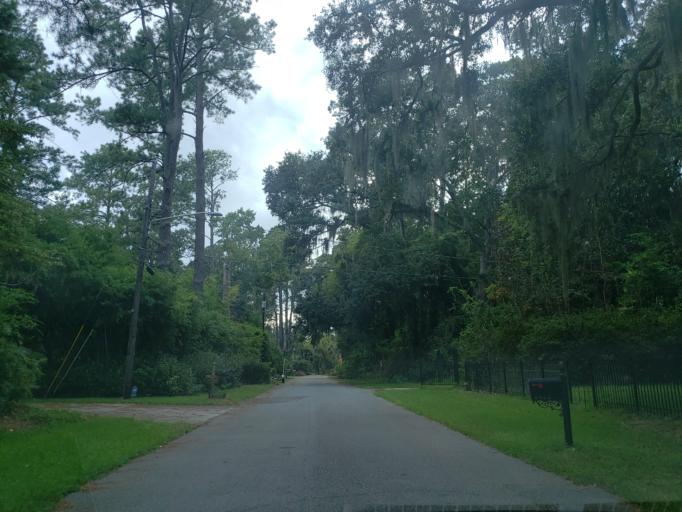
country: US
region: Georgia
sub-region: Chatham County
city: Isle of Hope
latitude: 31.9913
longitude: -81.0659
